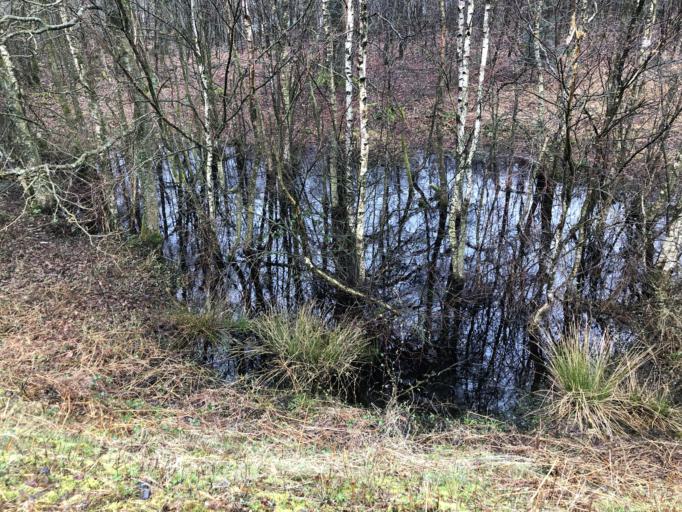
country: DK
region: South Denmark
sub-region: Aabenraa Kommune
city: Krusa
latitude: 54.9276
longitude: 9.4347
